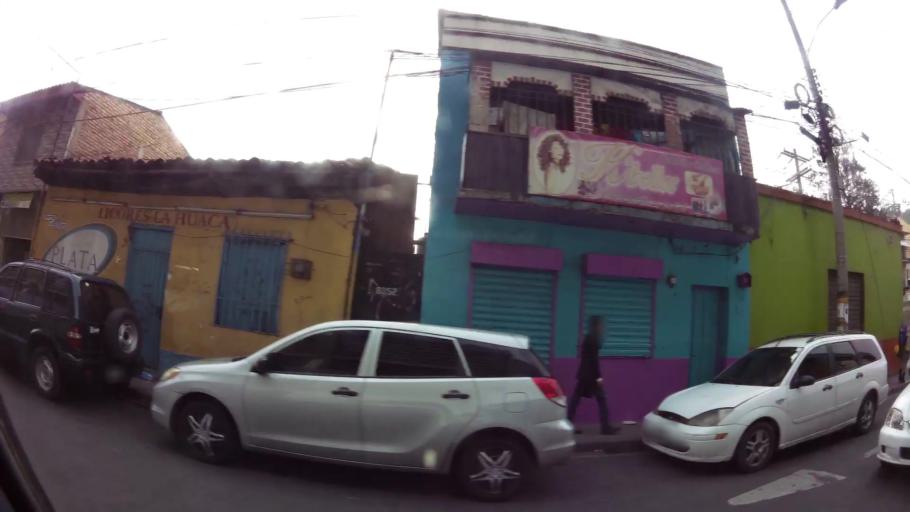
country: HN
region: Francisco Morazan
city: Tegucigalpa
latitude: 14.0983
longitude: -87.2032
